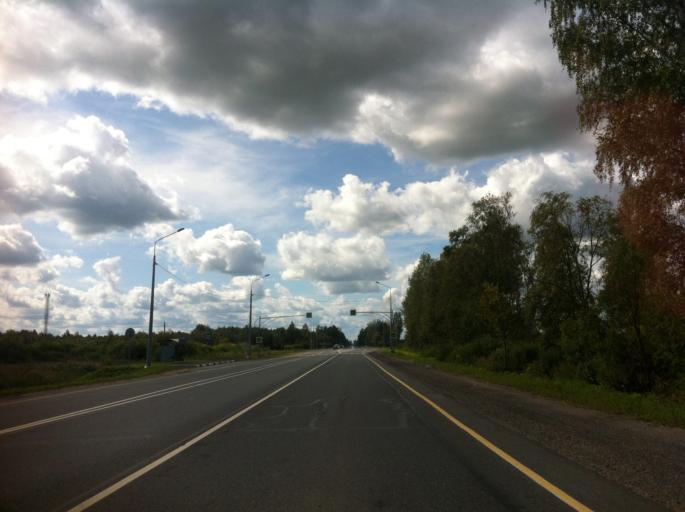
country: RU
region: Pskov
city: Pskov
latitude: 57.7721
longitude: 28.1328
